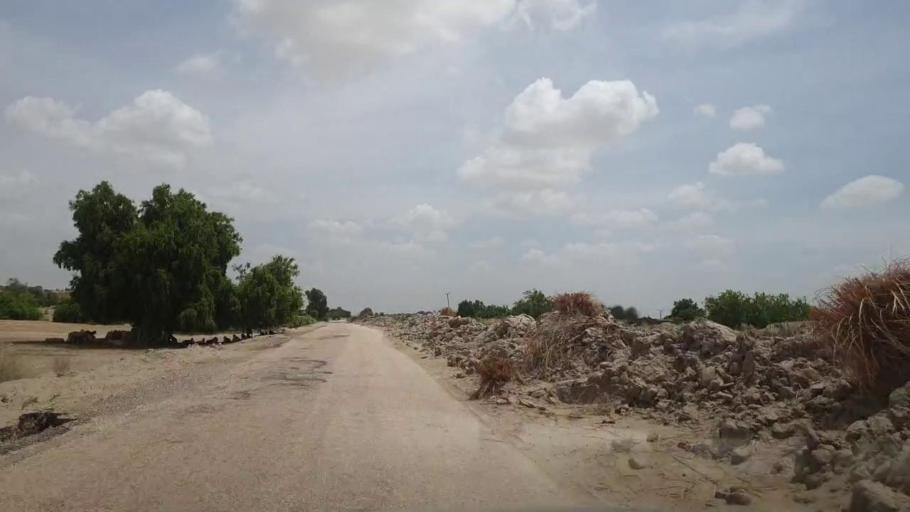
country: PK
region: Sindh
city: Kot Diji
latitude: 27.2126
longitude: 69.1132
